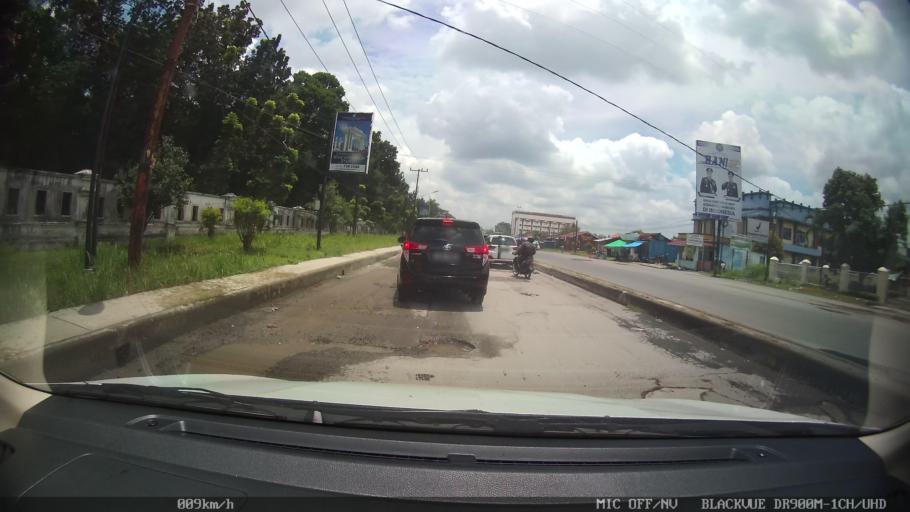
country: ID
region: North Sumatra
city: Medan
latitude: 3.6062
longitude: 98.7178
